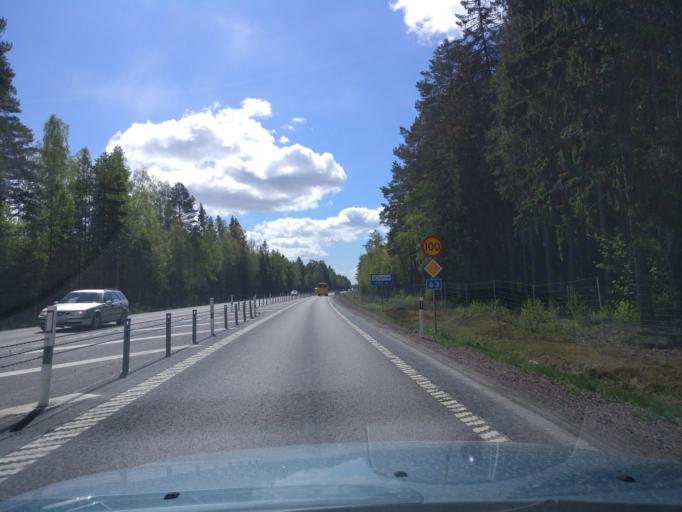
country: SE
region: Vaermland
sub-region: Karlstads Kommun
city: Karlstad
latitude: 59.4364
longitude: 13.5419
